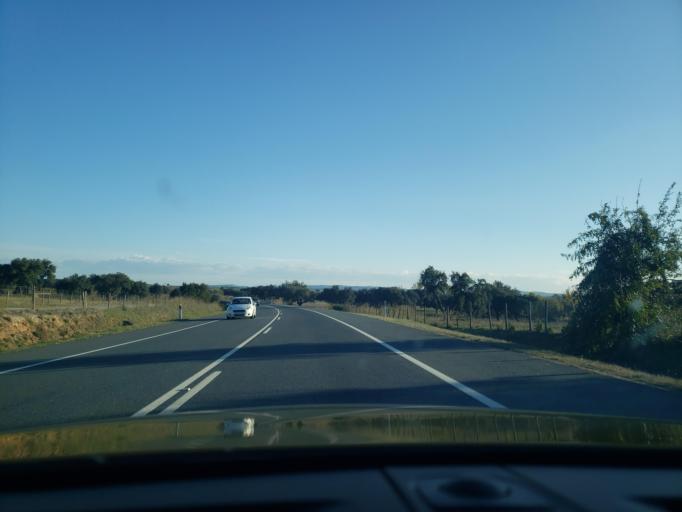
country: PT
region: Evora
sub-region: Portel
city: Portel
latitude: 38.4329
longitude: -7.7231
